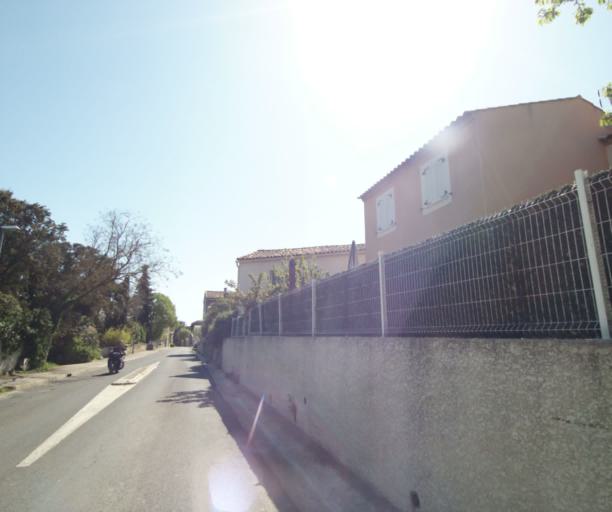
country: FR
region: Languedoc-Roussillon
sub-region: Departement de l'Herault
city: Sussargues
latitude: 43.7103
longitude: 4.0057
